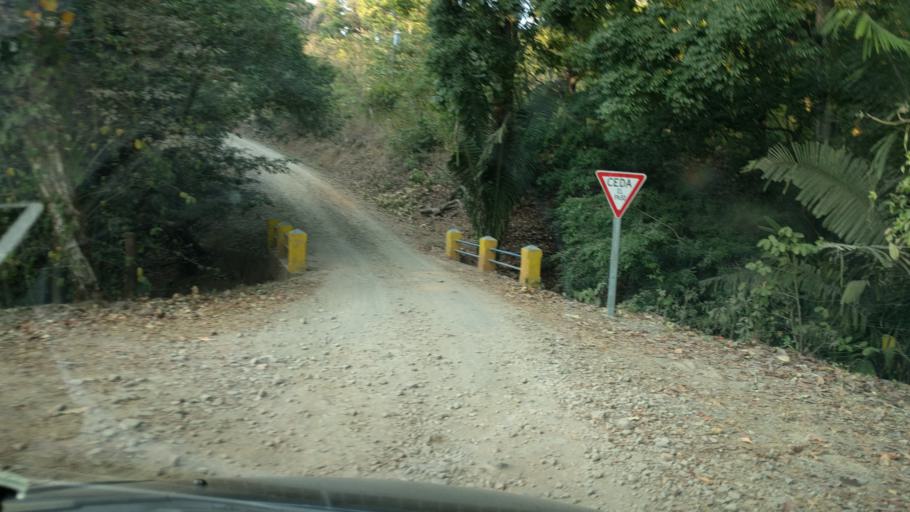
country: CR
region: Puntarenas
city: Esparza
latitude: 10.0195
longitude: -84.6962
